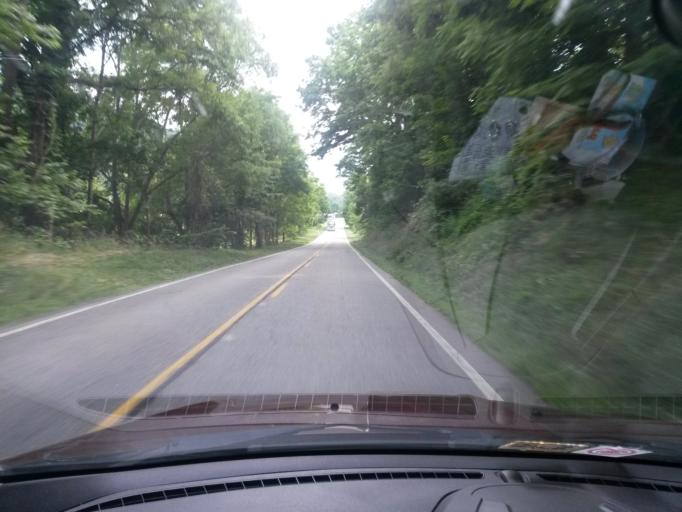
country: US
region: Virginia
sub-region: Highland County
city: Monterey
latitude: 38.4910
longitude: -79.5022
